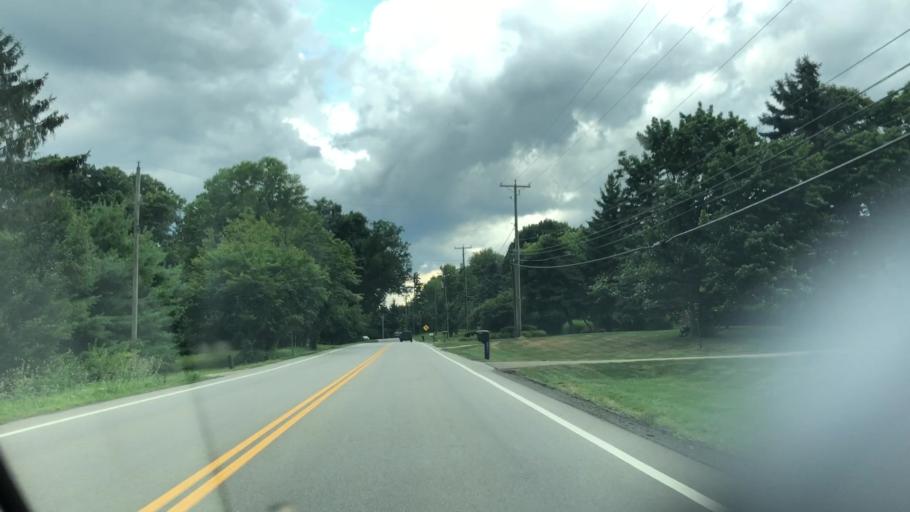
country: US
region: Ohio
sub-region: Stark County
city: Perry Heights
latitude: 40.8589
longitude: -81.4695
